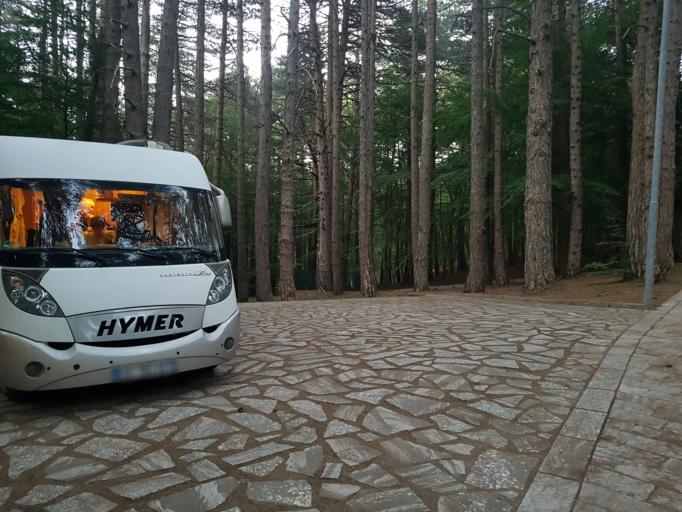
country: IT
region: Calabria
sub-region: Provincia di Reggio Calabria
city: Sant'Eufemia d'Aspromonte
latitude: 38.2019
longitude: 15.8567
